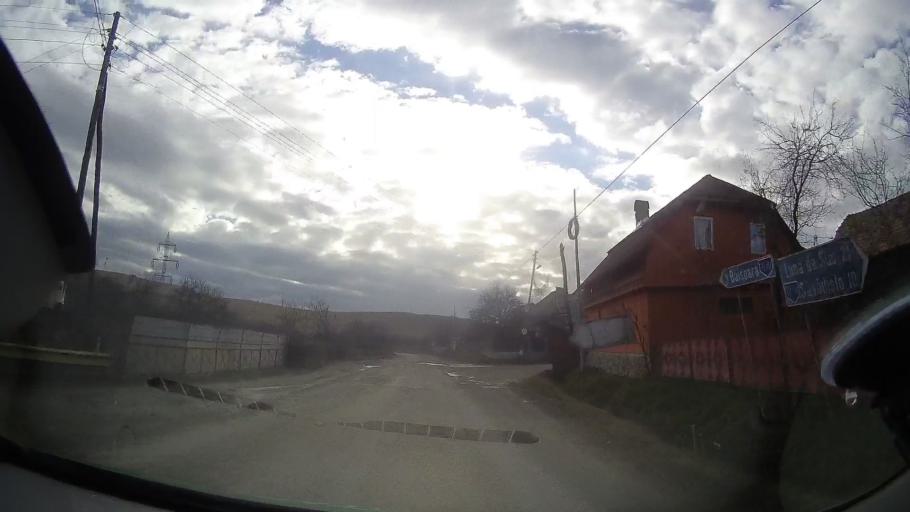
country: RO
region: Cluj
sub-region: Comuna Baisoara
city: Baisoara
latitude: 46.6014
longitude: 23.4620
